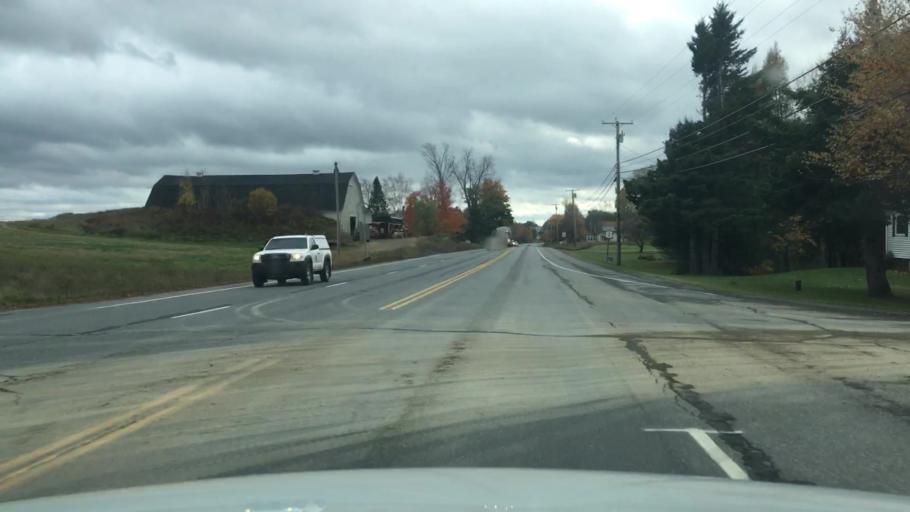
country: US
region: Maine
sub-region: Aroostook County
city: Houlton
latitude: 46.2171
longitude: -67.8410
